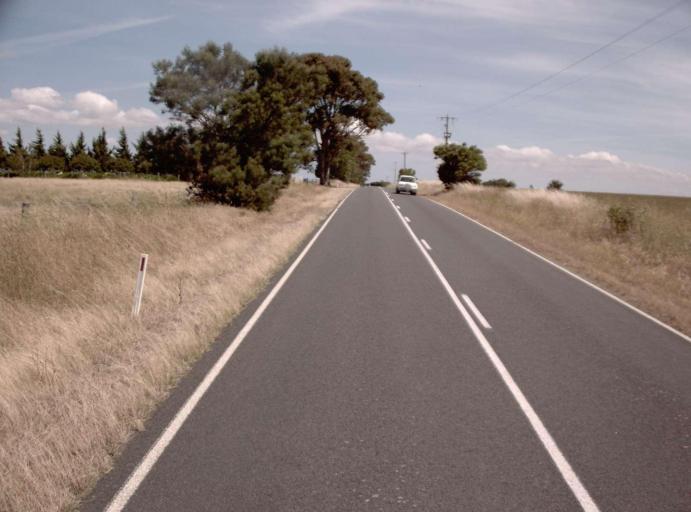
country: AU
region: Victoria
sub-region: Wellington
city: Heyfield
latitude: -38.1134
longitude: 146.8616
